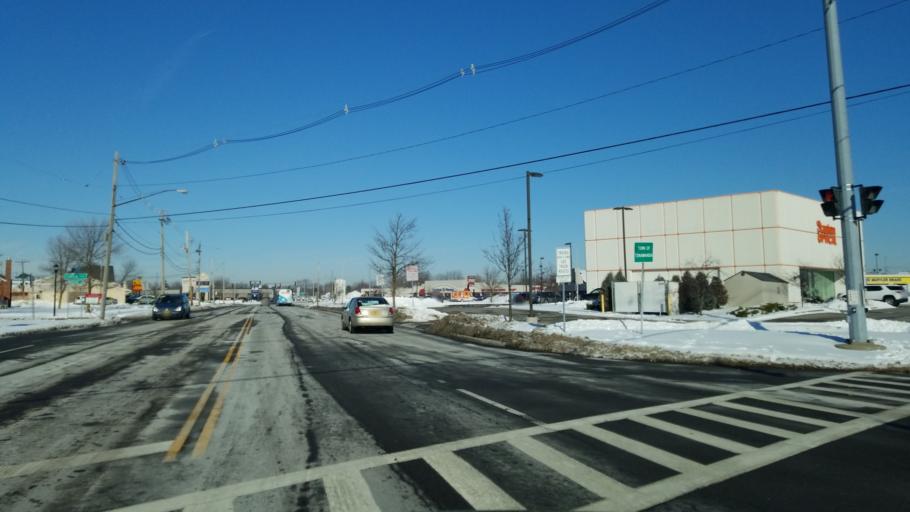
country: US
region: New York
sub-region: Erie County
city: Amherst
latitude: 42.9798
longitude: -78.8232
